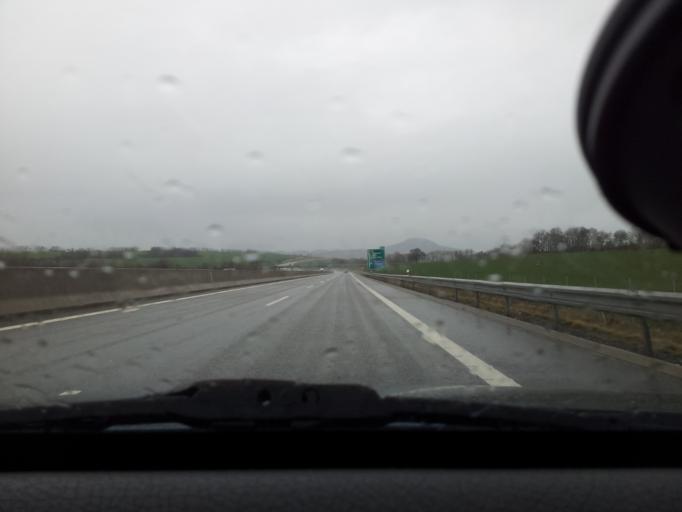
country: SK
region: Nitriansky
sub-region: Okres Nitra
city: Vrable
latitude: 48.3319
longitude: 18.2809
